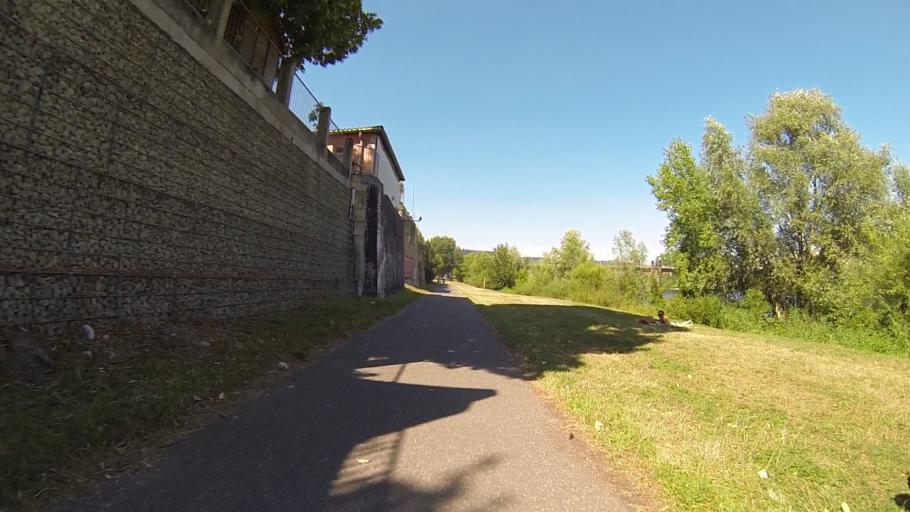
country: DE
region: Rheinland-Pfalz
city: Trier
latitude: 49.7501
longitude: 6.6251
